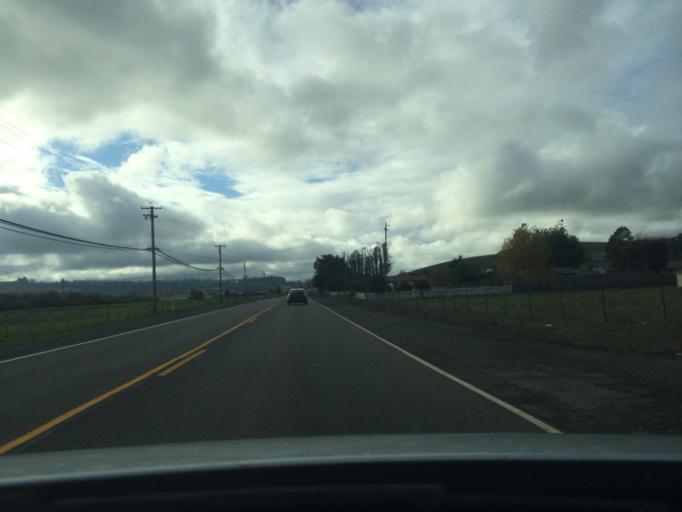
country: US
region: California
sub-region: Sonoma County
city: Cotati
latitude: 38.2583
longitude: -122.7604
